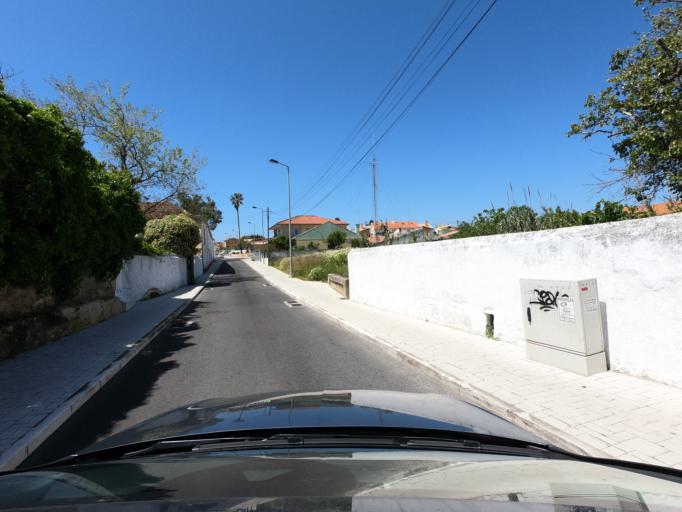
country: PT
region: Lisbon
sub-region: Cascais
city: Parede
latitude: 38.7138
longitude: -9.3503
